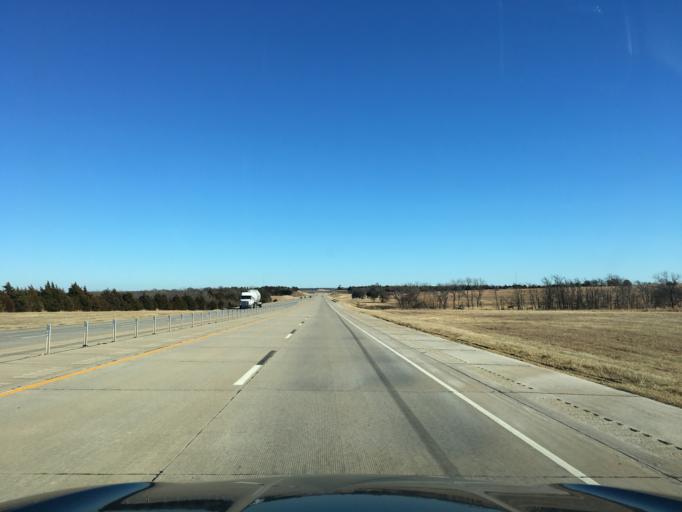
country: US
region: Oklahoma
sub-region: Payne County
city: Yale
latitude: 36.2251
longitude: -96.6340
